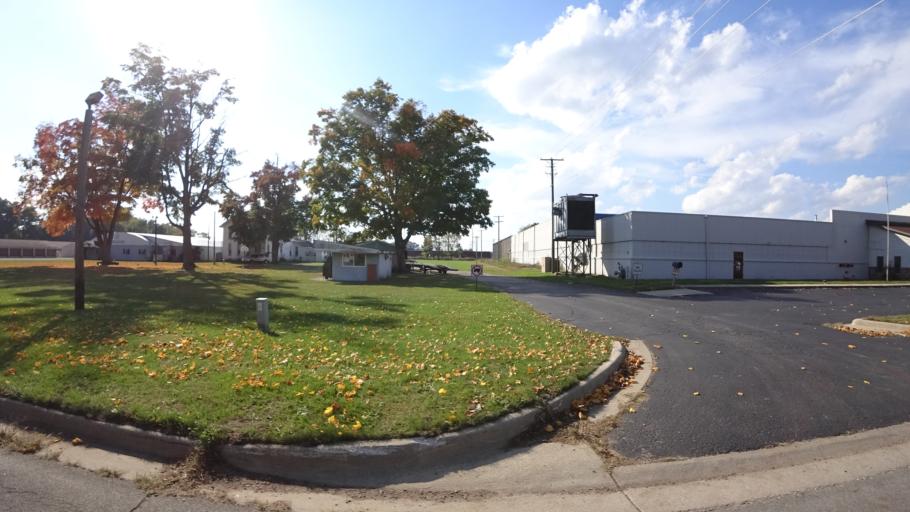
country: US
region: Michigan
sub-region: Saint Joseph County
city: Three Rivers
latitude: 41.9619
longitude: -85.6348
